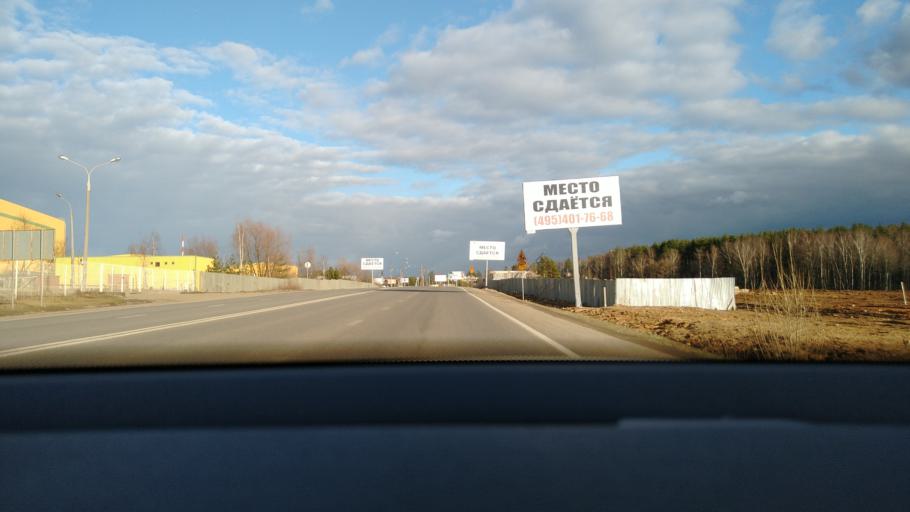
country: RU
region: Moskovskaya
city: Pavlovskaya Sloboda
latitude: 55.8126
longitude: 37.1137
